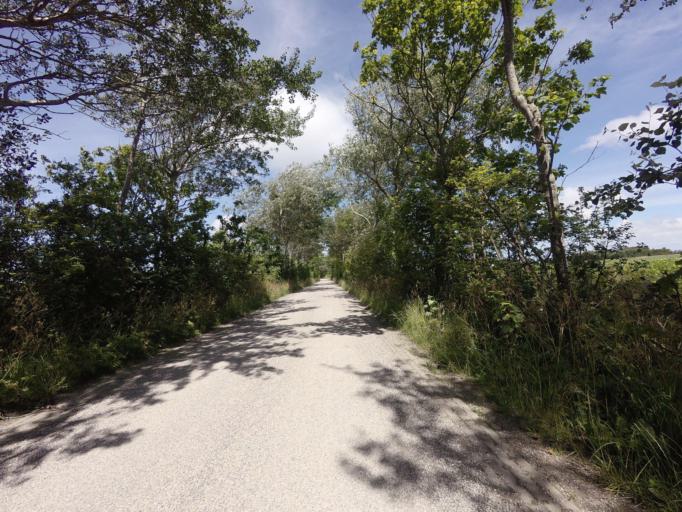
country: NL
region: North Holland
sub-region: Gemeente Texel
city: Den Burg
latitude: 53.0639
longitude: 4.8089
